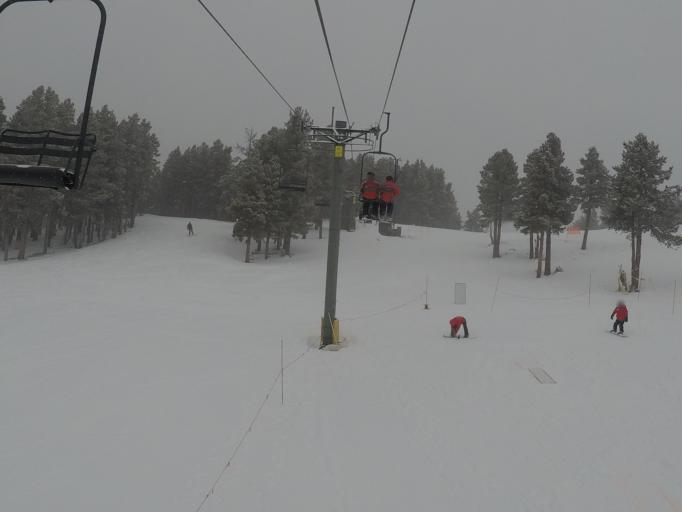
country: US
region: Montana
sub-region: Carbon County
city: Red Lodge
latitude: 45.1935
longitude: -109.3423
